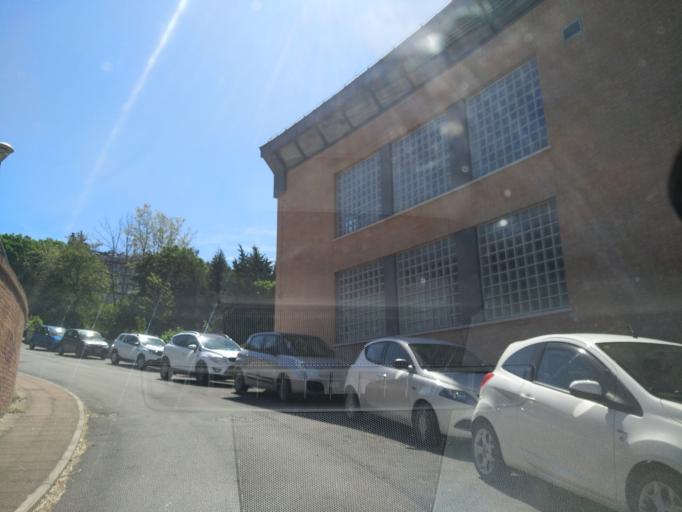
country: IT
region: The Marches
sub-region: Provincia di Pesaro e Urbino
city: Urbino
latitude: 43.7354
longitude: 12.6281
